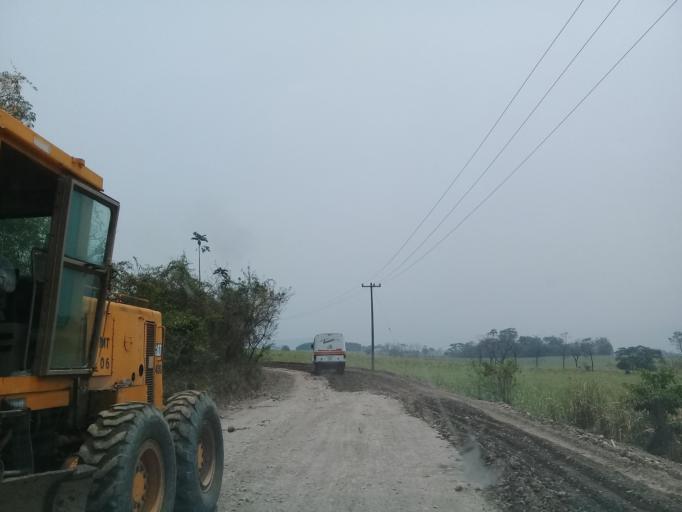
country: MX
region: Veracruz
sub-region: Tezonapa
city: Laguna Chica (Pueblo Nuevo)
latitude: 18.5421
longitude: -96.7381
